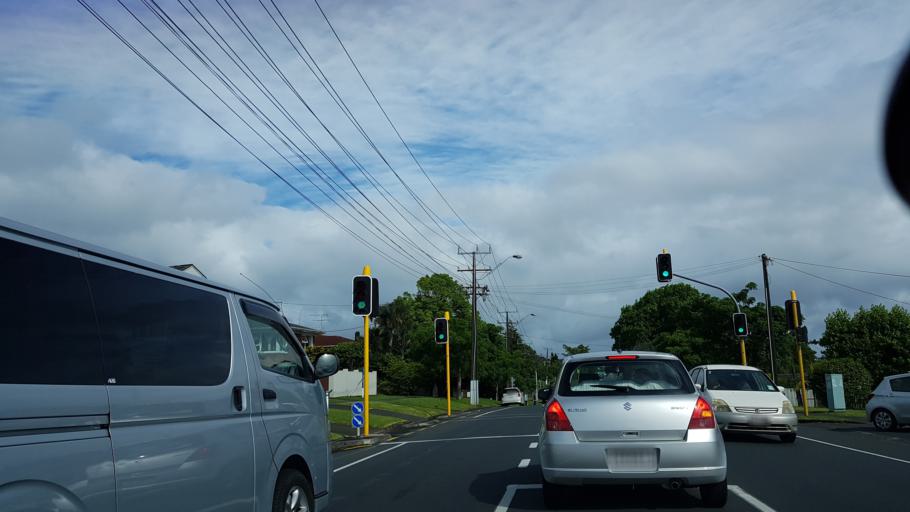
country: NZ
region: Auckland
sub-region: Auckland
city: North Shore
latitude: -36.7896
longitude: 174.7449
